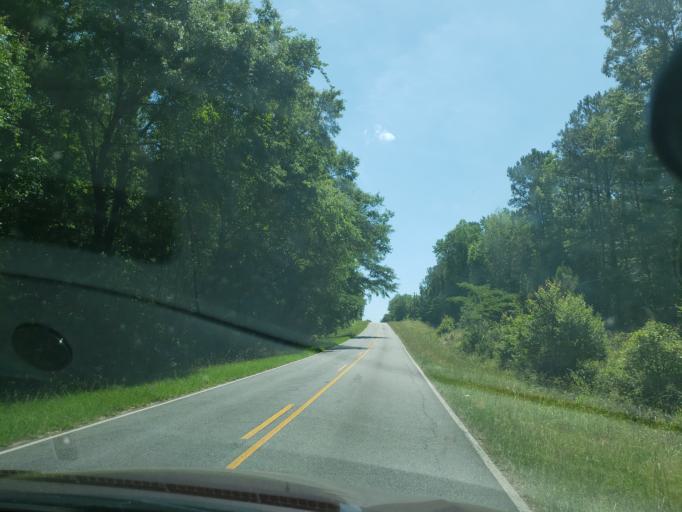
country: US
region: Alabama
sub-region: Elmore County
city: Tallassee
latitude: 32.5809
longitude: -85.8194
